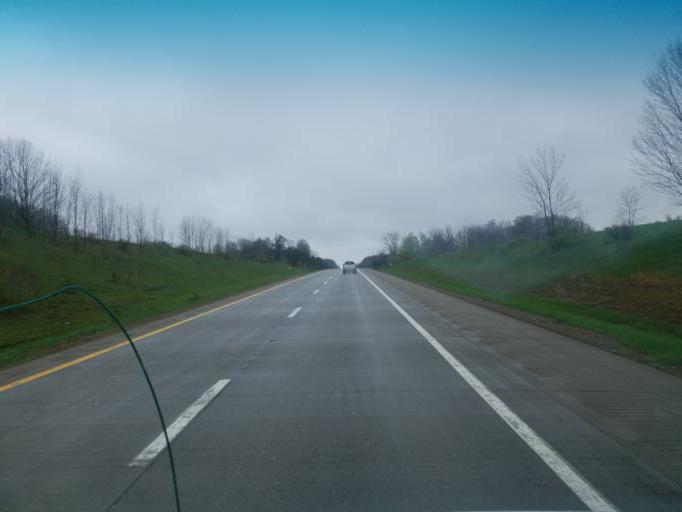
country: US
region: New York
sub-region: Chautauqua County
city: Clymer
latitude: 42.1471
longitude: -79.6213
